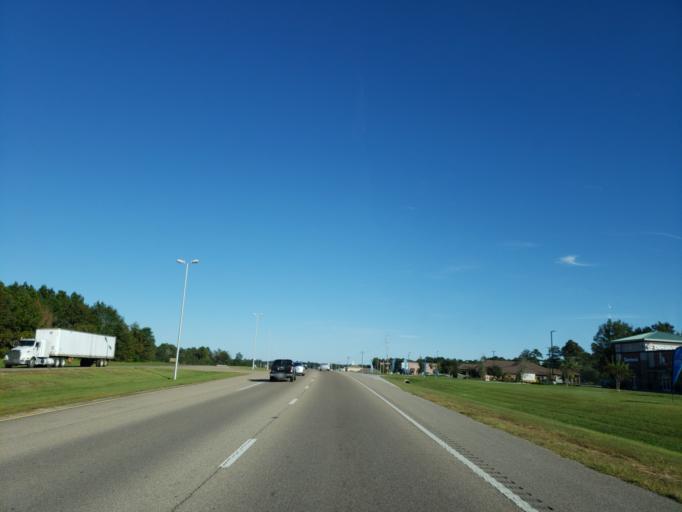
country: US
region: Mississippi
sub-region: Forrest County
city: Petal
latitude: 31.3524
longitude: -89.2480
